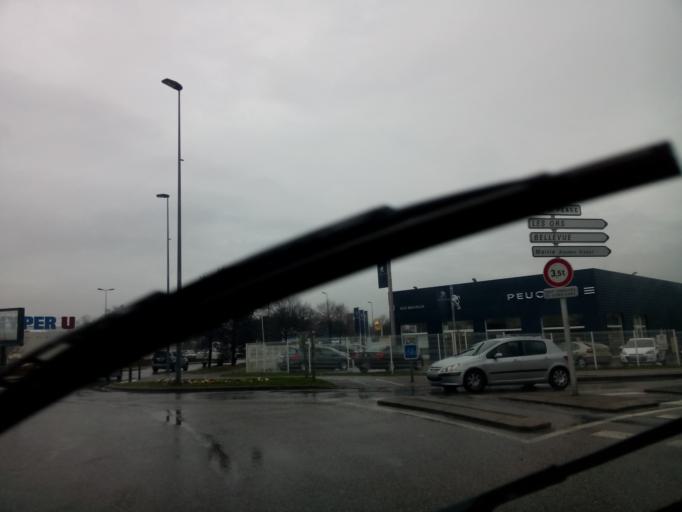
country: FR
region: Rhone-Alpes
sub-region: Departement de la Drome
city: Romans-sur-Isere
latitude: 45.0433
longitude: 5.0295
